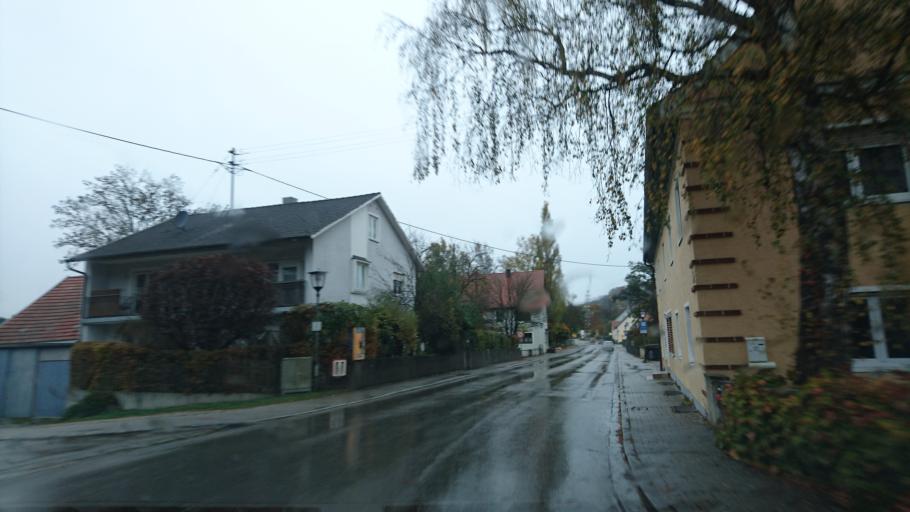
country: DE
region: Bavaria
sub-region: Upper Bavaria
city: Jetzendorf
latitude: 48.4347
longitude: 11.4181
